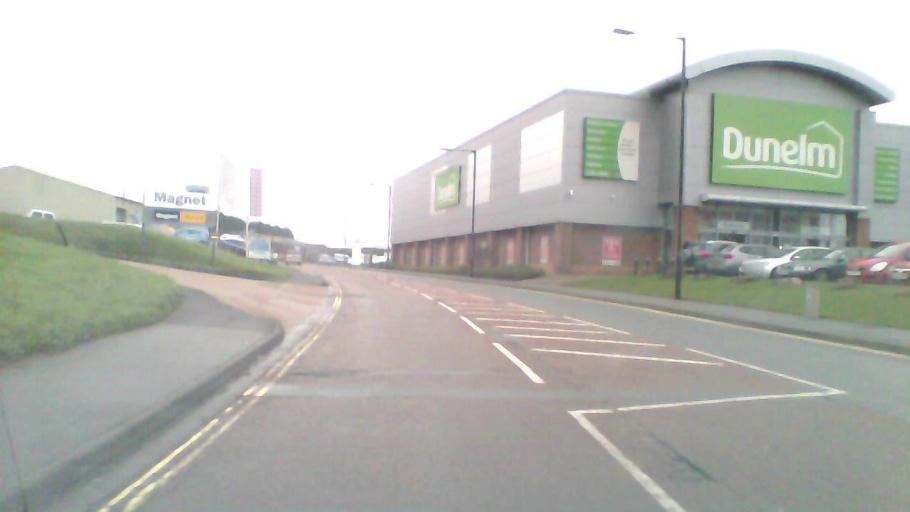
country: GB
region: England
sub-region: Isle of Wight
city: Newport
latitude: 50.7042
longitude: -1.2938
